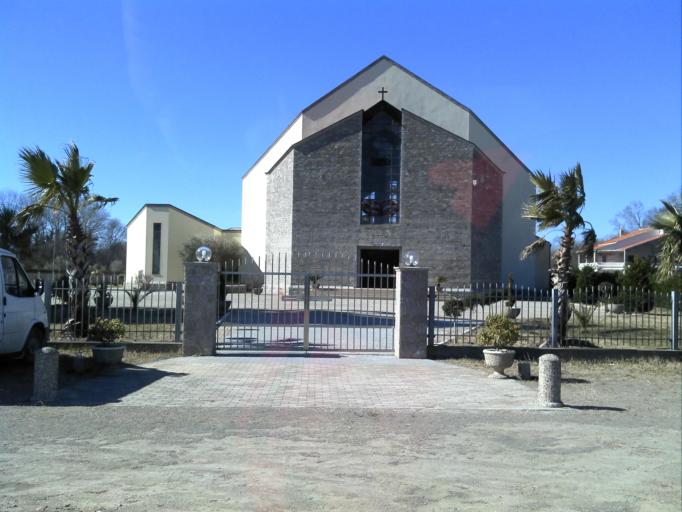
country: AL
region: Shkoder
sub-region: Rrethi i Shkodres
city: Velipoje
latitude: 41.8729
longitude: 19.4041
